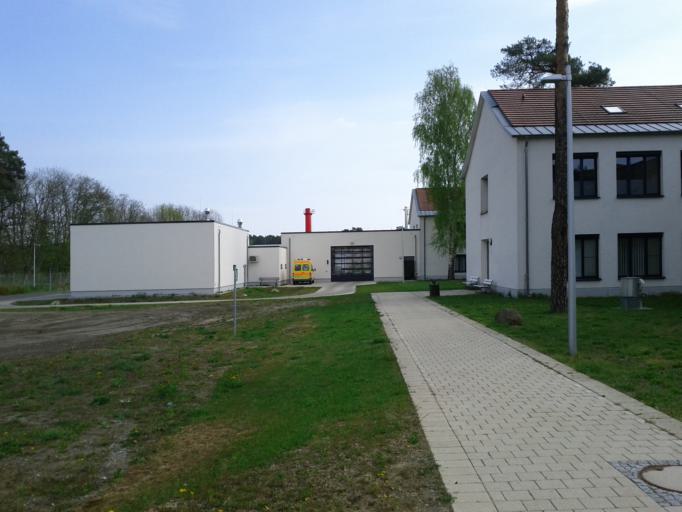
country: DE
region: Brandenburg
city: Bad Saarow
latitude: 52.2831
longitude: 14.0603
